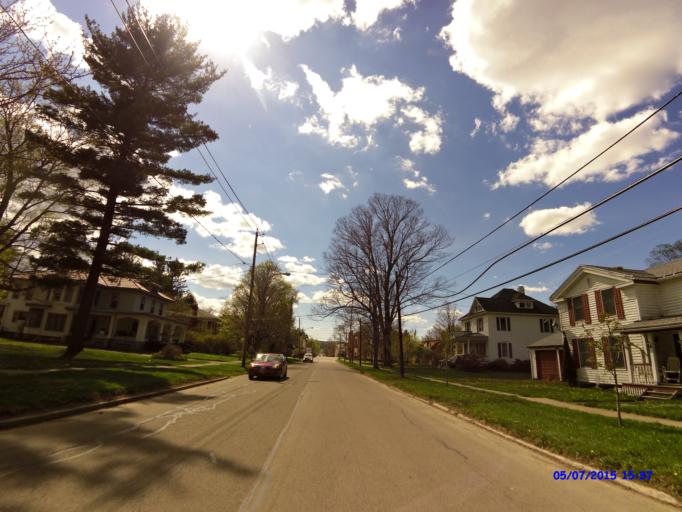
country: US
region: New York
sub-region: Cattaraugus County
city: Franklinville
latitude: 42.3372
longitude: -78.4553
